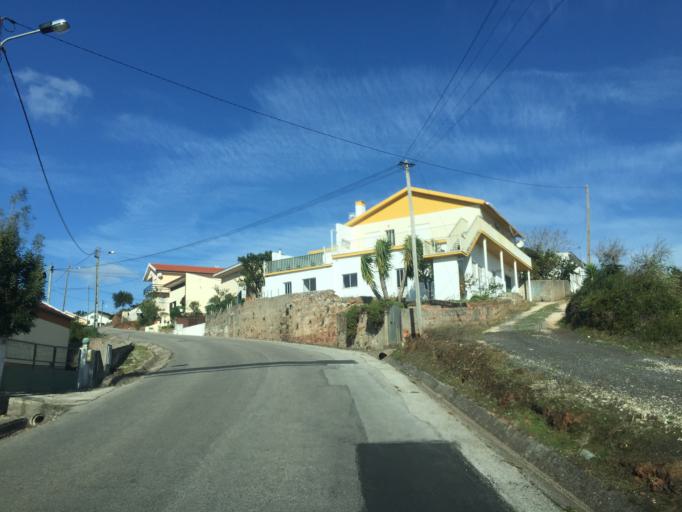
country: PT
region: Coimbra
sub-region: Figueira da Foz
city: Tavarede
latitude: 40.1707
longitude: -8.8397
